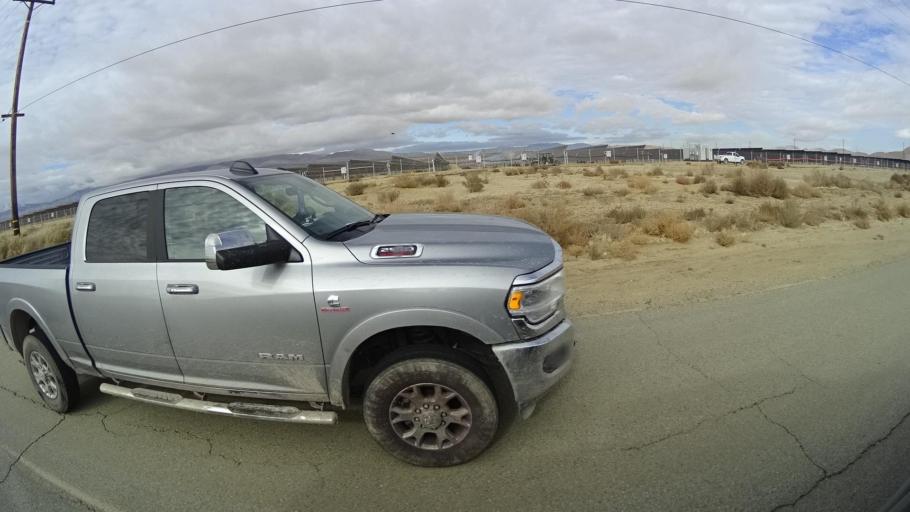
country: US
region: California
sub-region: Kern County
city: Rosamond
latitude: 34.8632
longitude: -118.3295
